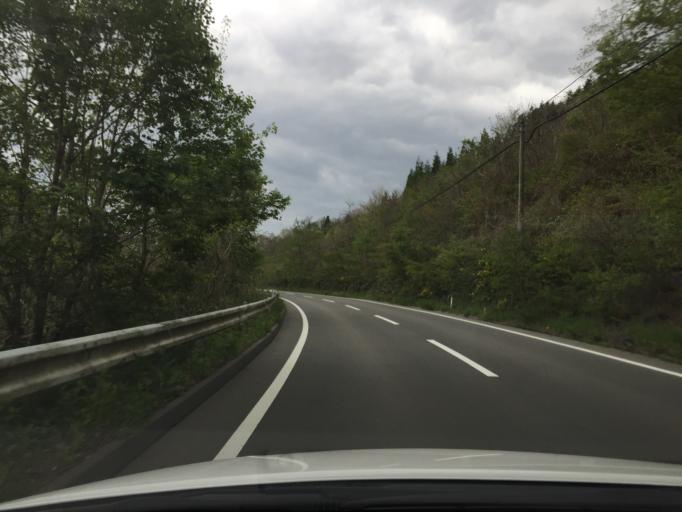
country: JP
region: Fukushima
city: Yanagawamachi-saiwaicho
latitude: 37.7279
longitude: 140.7333
